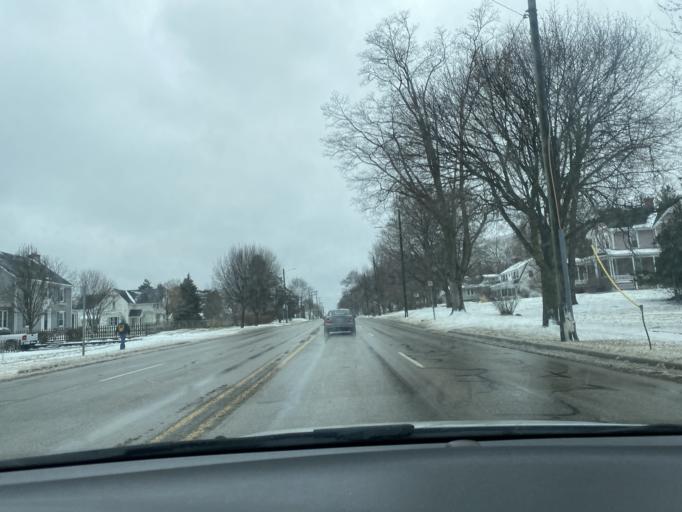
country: US
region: Michigan
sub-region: Lapeer County
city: Lapeer
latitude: 43.0507
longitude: -83.3221
